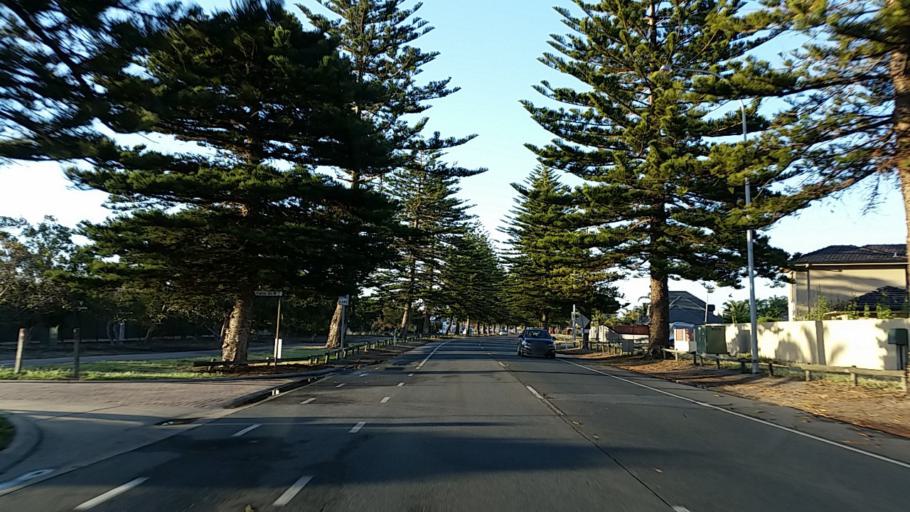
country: AU
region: South Australia
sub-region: Port Adelaide Enfield
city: Birkenhead
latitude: -34.7894
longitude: 138.4903
